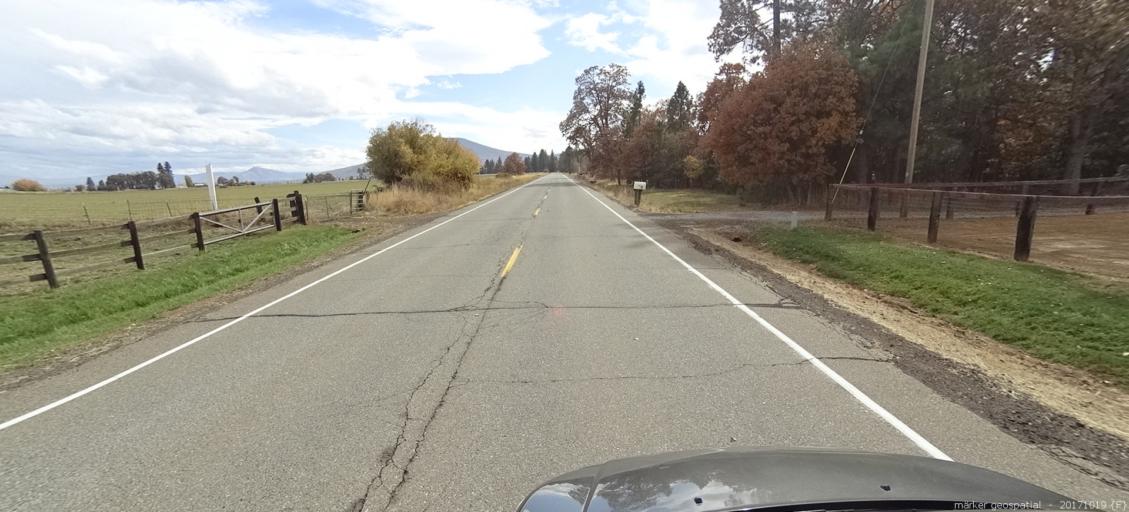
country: US
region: California
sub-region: Shasta County
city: Burney
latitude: 41.0874
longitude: -121.5144
